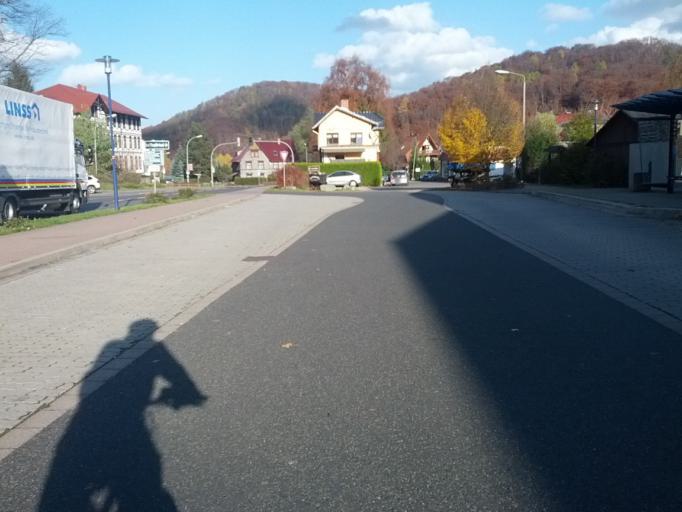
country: DE
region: Thuringia
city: Thal
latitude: 50.9184
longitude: 10.3923
